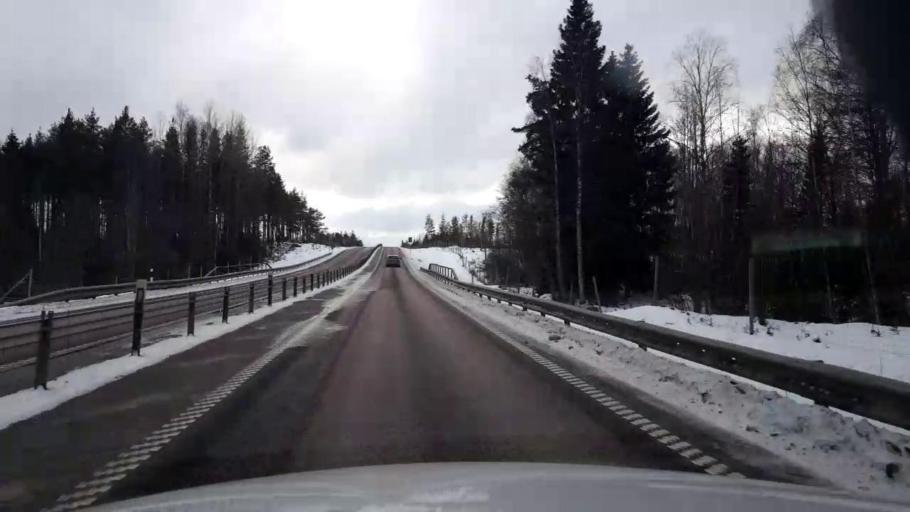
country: SE
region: Gaevleborg
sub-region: Hudiksvalls Kommun
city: Hudiksvall
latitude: 61.8210
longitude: 17.1908
